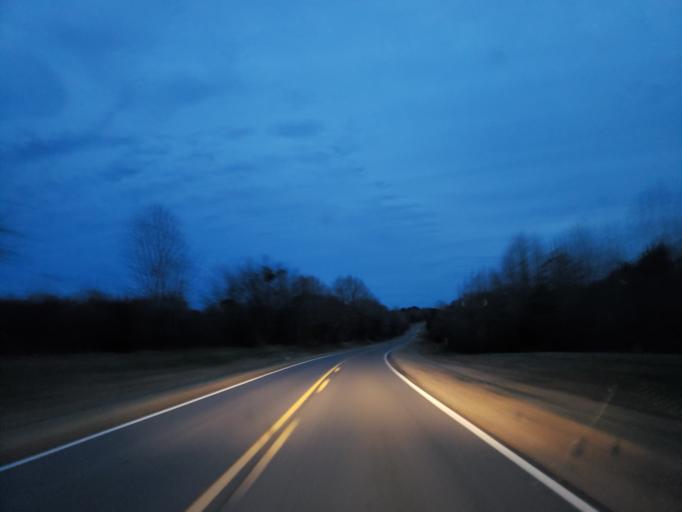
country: US
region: Alabama
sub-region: Greene County
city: Eutaw
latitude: 32.8968
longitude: -87.9598
